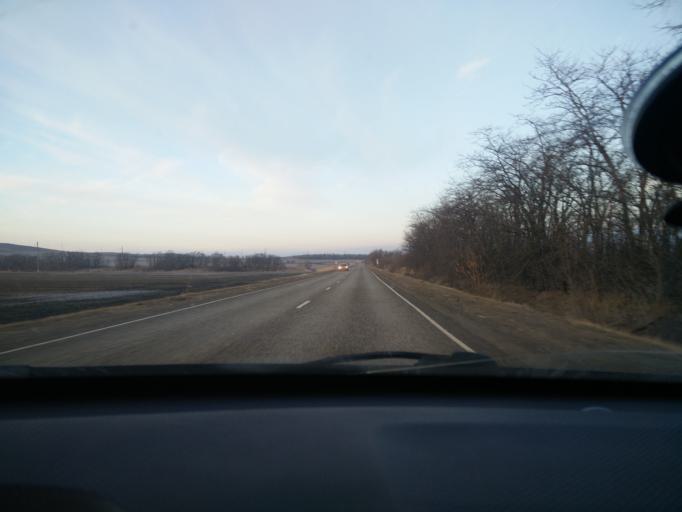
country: RU
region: Stavropol'skiy
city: Balakhonovskoye
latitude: 44.9949
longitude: 41.7278
